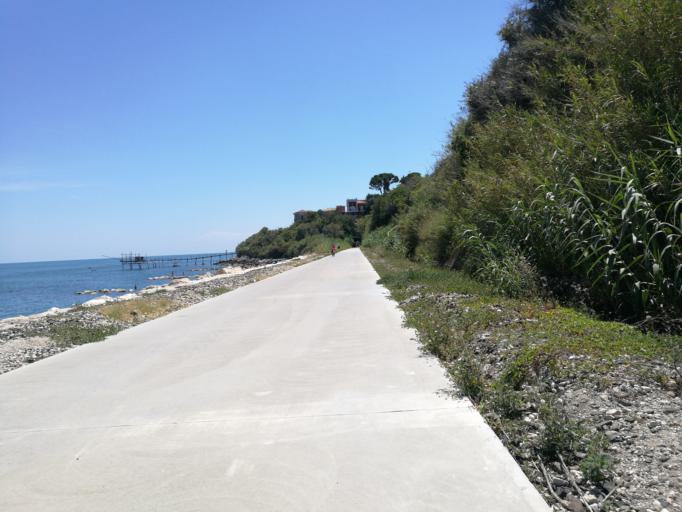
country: IT
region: Abruzzo
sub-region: Provincia di Chieti
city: Marina di San Vito
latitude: 42.3015
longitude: 14.4568
